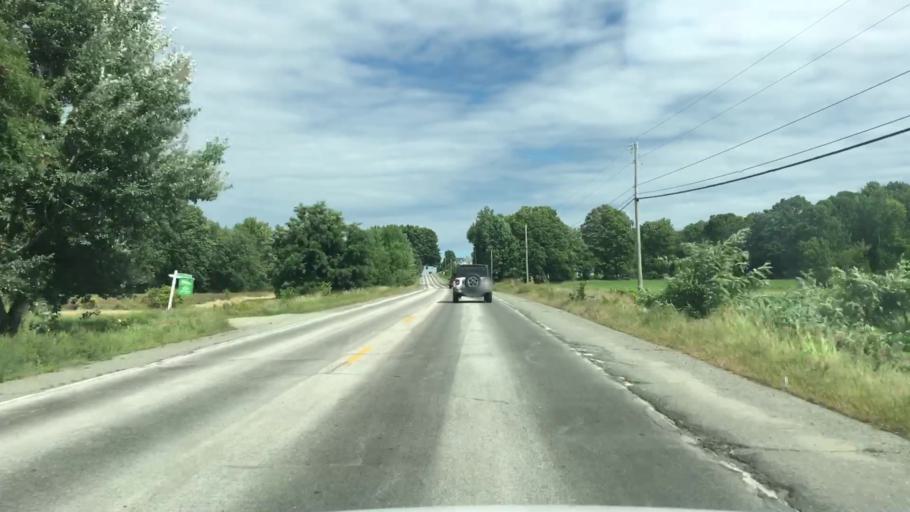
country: US
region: Maine
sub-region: Piscataquis County
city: Dover-Foxcroft
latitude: 45.1577
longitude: -69.2337
